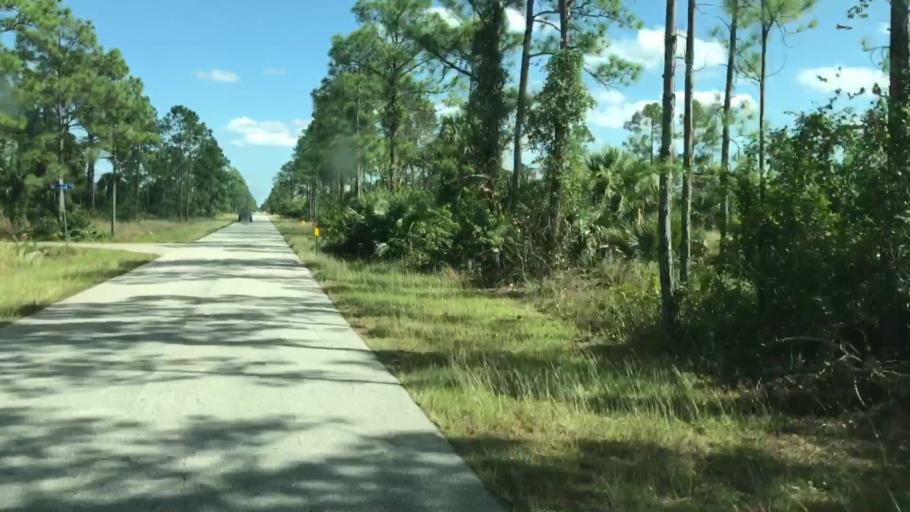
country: US
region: Florida
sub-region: Lee County
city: Lehigh Acres
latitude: 26.6283
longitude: -81.6412
